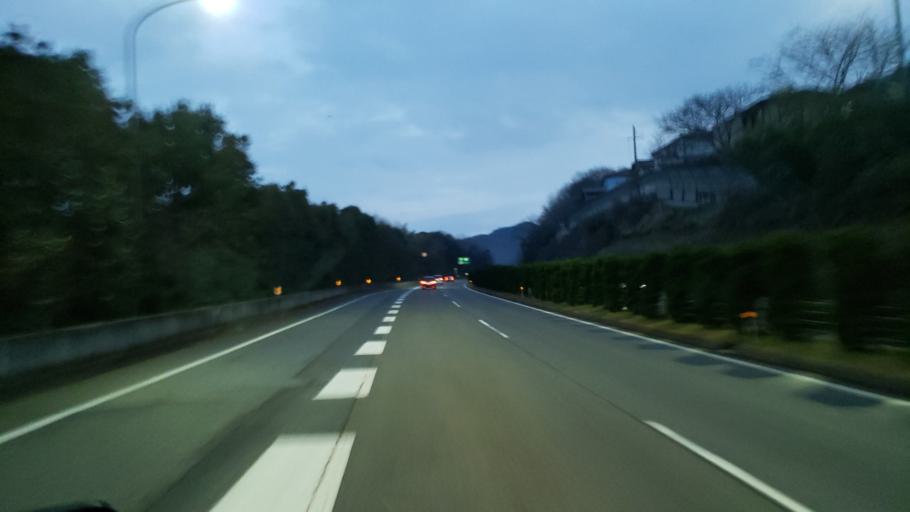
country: JP
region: Hyogo
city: Himeji
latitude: 34.8707
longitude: 134.7396
